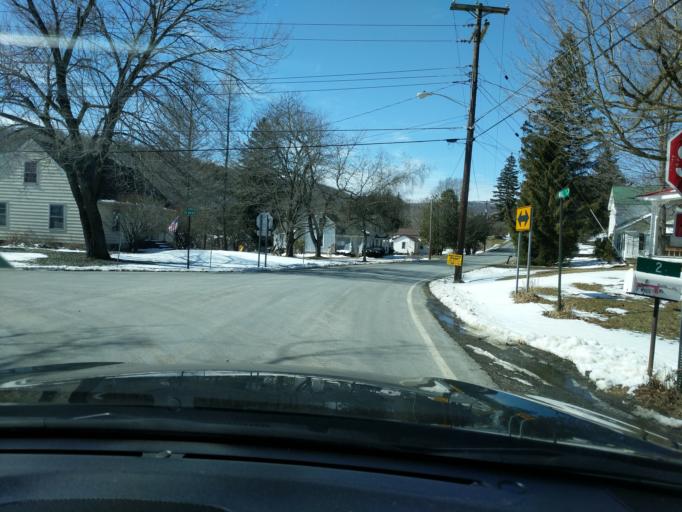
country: US
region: New York
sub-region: Tompkins County
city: Dryden
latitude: 42.3044
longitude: -76.2541
